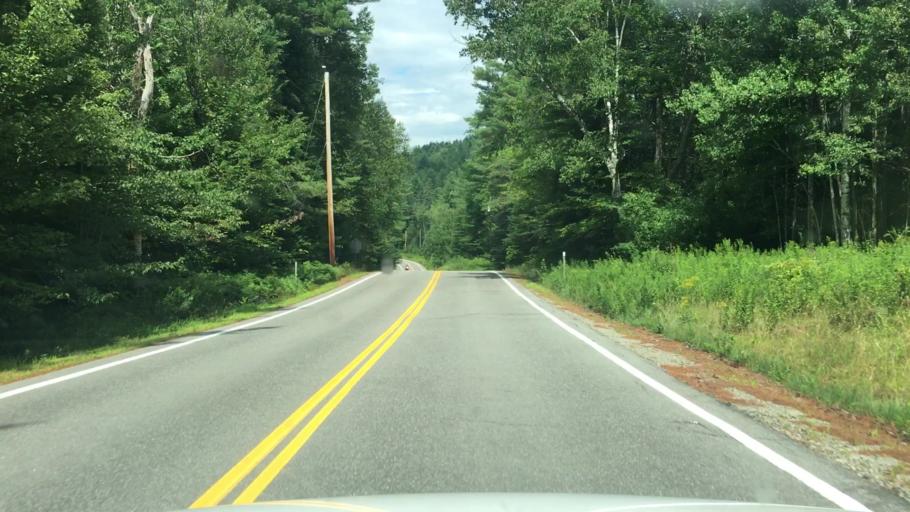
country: US
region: New Hampshire
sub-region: Coos County
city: Whitefield
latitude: 44.3130
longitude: -71.6567
